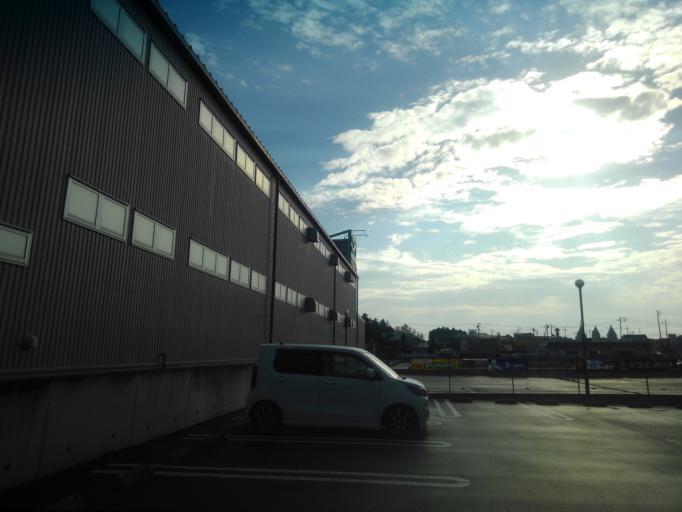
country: JP
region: Ibaraki
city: Naka
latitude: 36.0729
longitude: 140.0852
